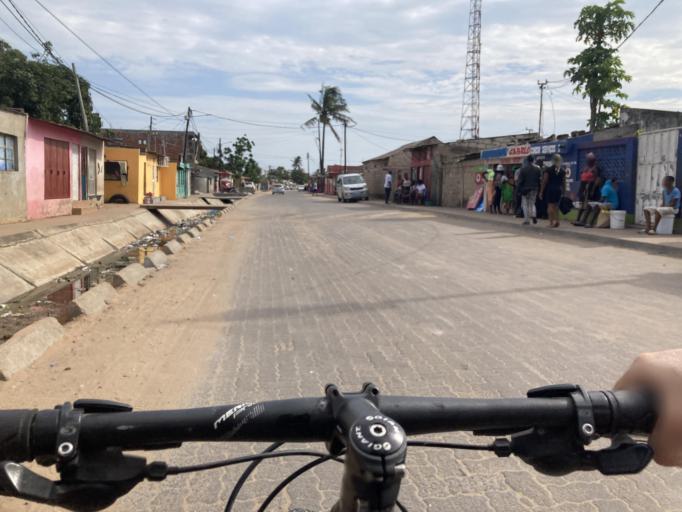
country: MZ
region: Maputo City
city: Maputo
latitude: -25.9403
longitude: 32.5841
